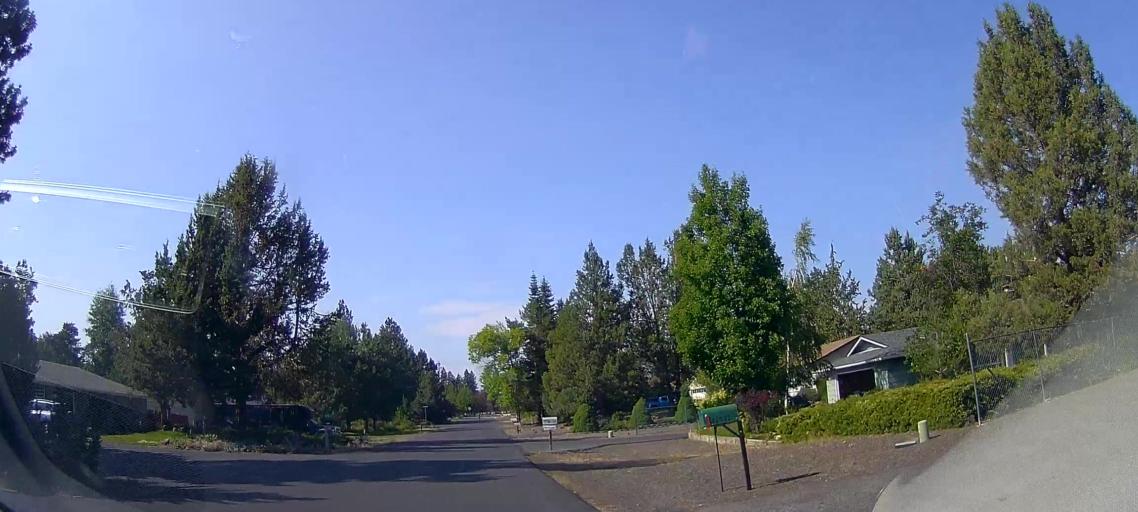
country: US
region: Oregon
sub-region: Deschutes County
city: Bend
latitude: 44.0357
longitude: -121.2813
